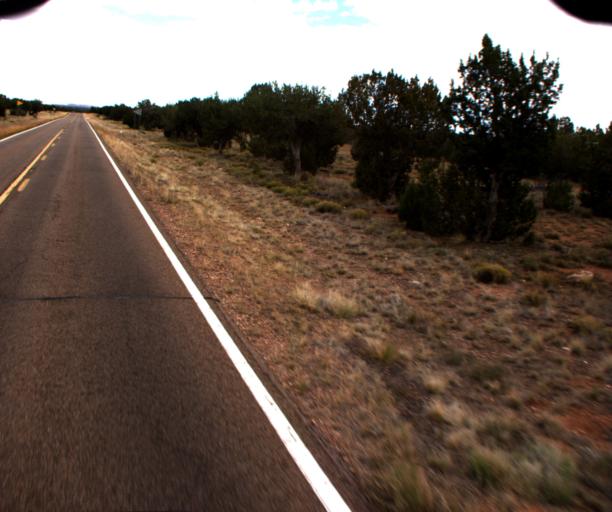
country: US
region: Arizona
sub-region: Navajo County
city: Heber-Overgaard
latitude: 34.5167
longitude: -110.4377
